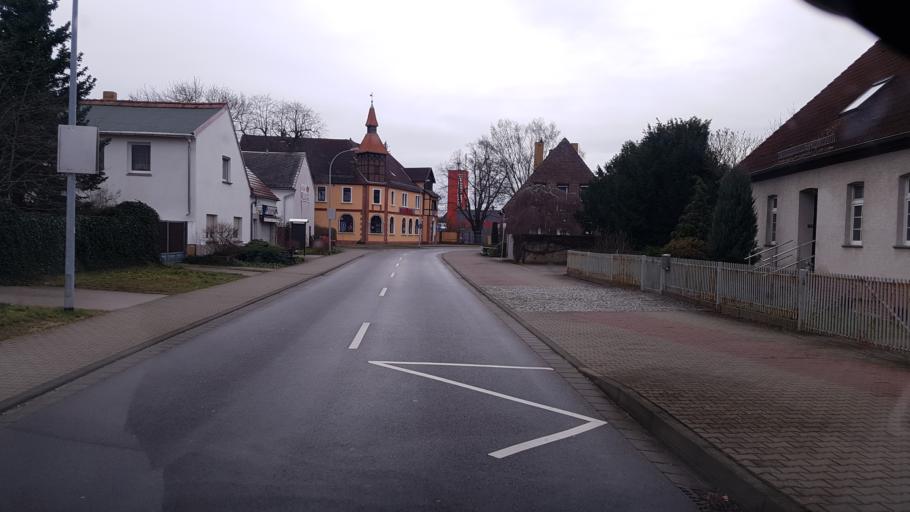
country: DE
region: Brandenburg
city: Ruhland
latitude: 51.4717
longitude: 13.8905
